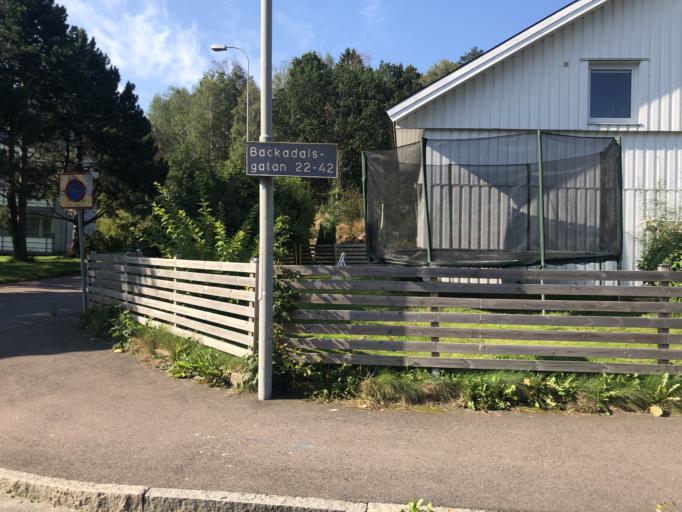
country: SE
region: Vaestra Goetaland
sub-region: Goteborg
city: Goeteborg
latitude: 57.7488
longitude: 11.9767
